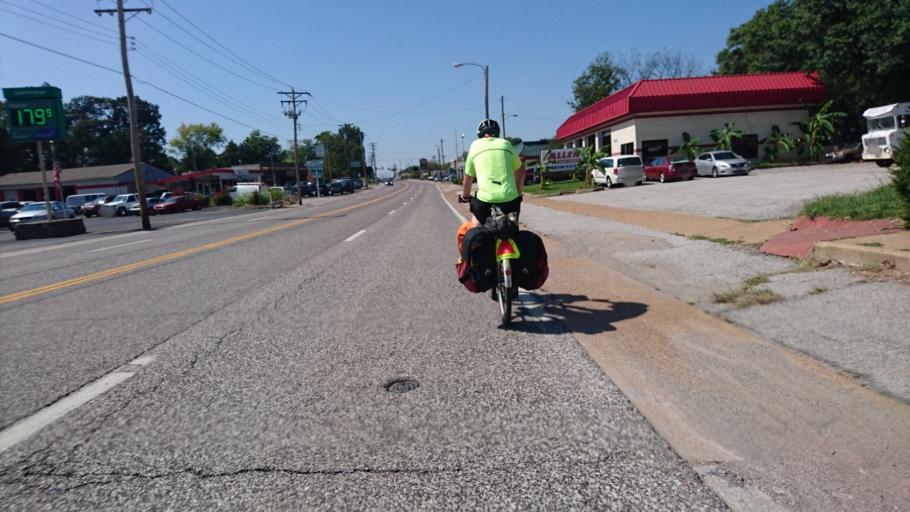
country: US
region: Missouri
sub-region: Saint Louis County
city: Rock Hill
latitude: 38.6082
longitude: -90.3699
